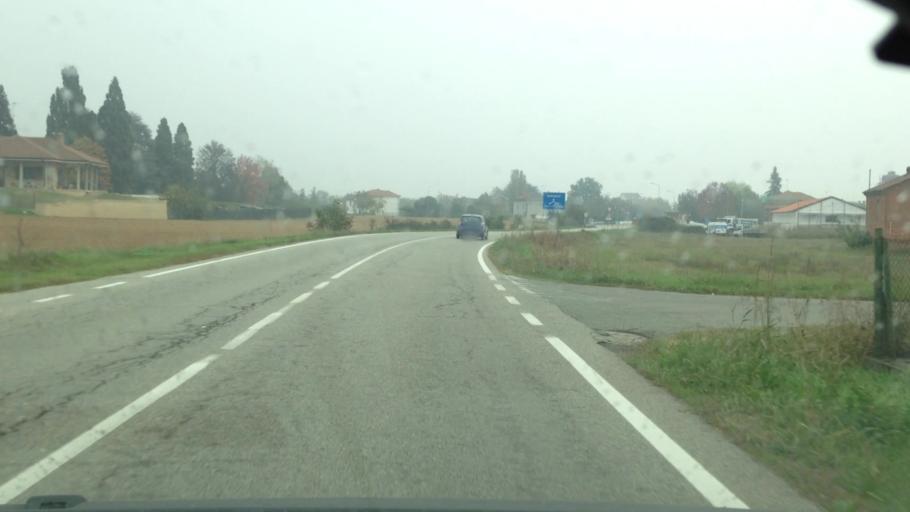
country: IT
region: Piedmont
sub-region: Provincia di Alessandria
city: Felizzano
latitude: 44.9010
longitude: 8.4355
